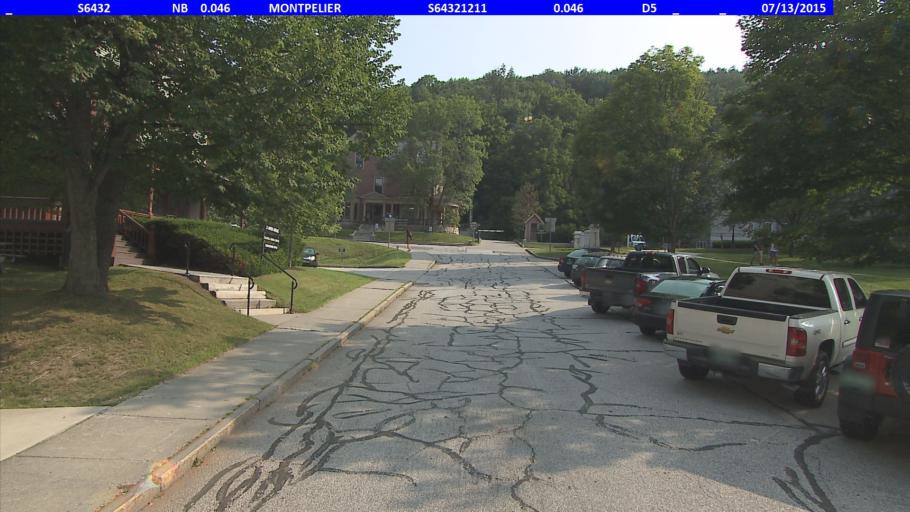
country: US
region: Vermont
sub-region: Washington County
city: Montpelier
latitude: 44.2622
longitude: -72.5815
